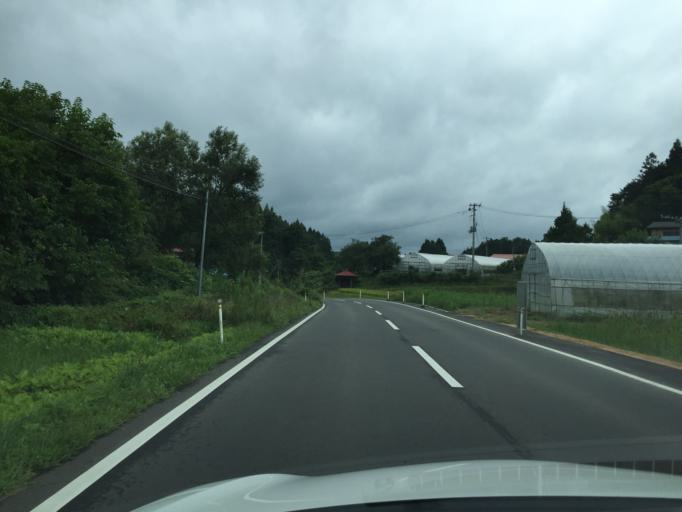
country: JP
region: Fukushima
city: Funehikimachi-funehiki
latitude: 37.4602
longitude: 140.5375
